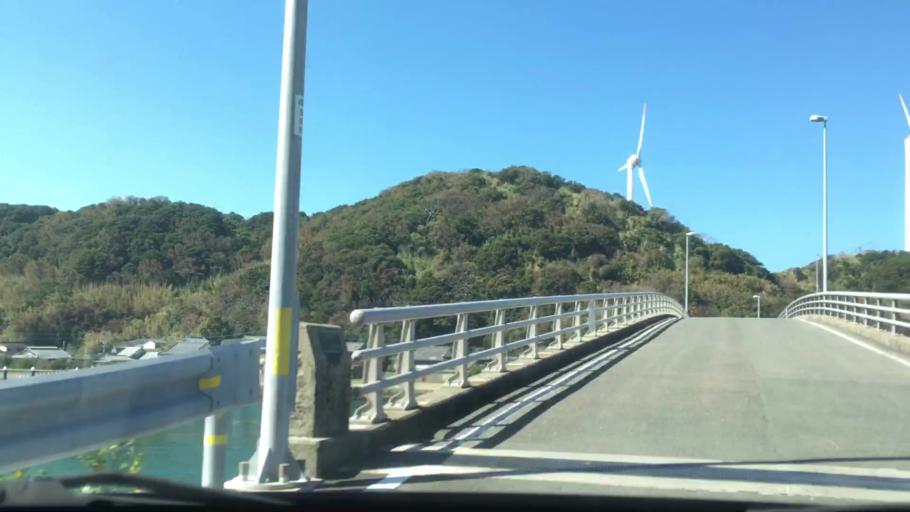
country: JP
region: Nagasaki
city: Sasebo
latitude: 33.0039
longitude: 129.5552
